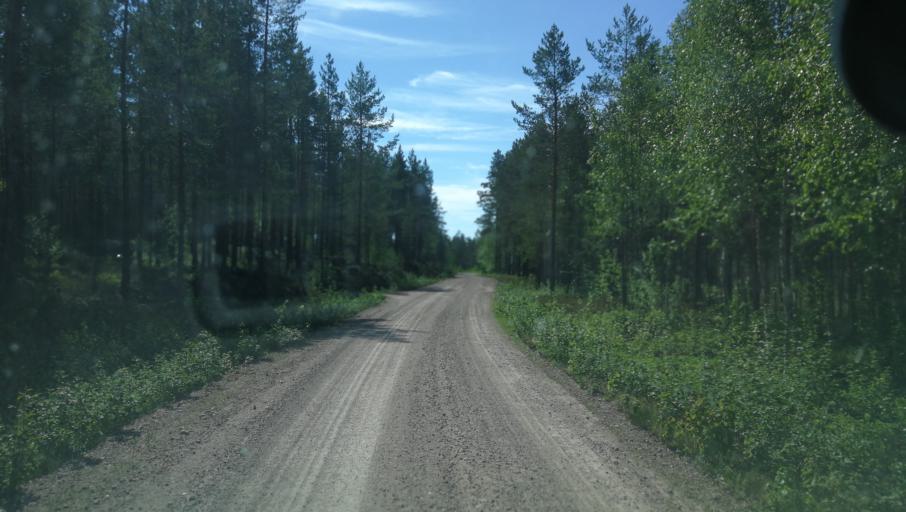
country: SE
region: Dalarna
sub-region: Vansbro Kommun
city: Vansbro
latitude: 60.8377
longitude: 14.1501
